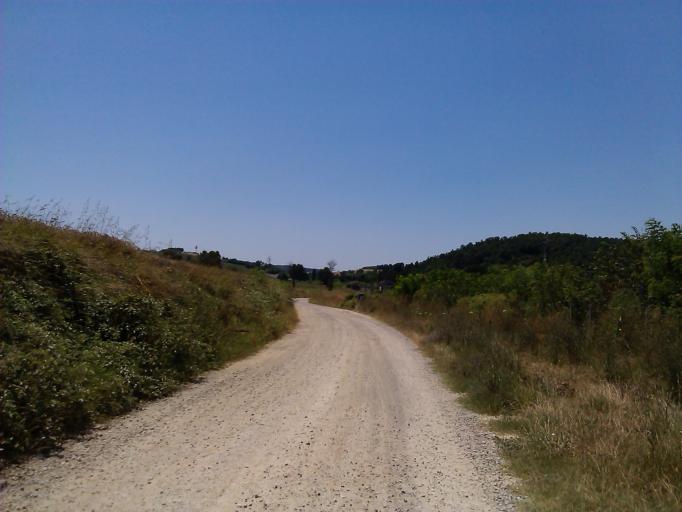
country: IT
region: Umbria
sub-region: Provincia di Terni
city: Fabro Scalo
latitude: 42.8507
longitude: 12.0408
